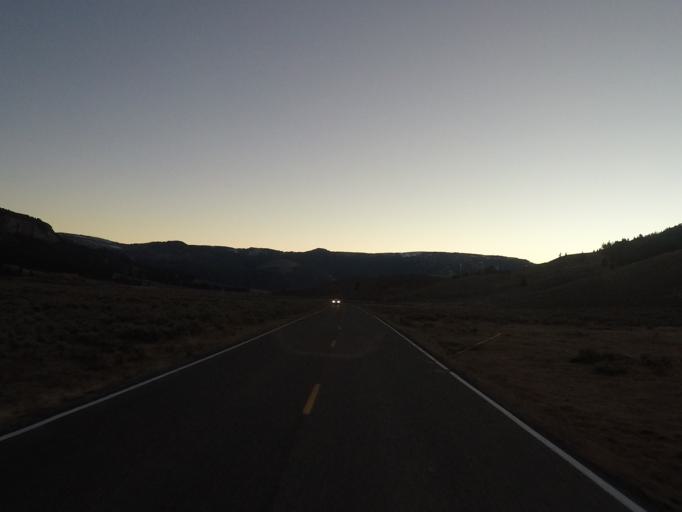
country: US
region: Montana
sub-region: Park County
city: Livingston
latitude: 44.8886
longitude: -110.1408
